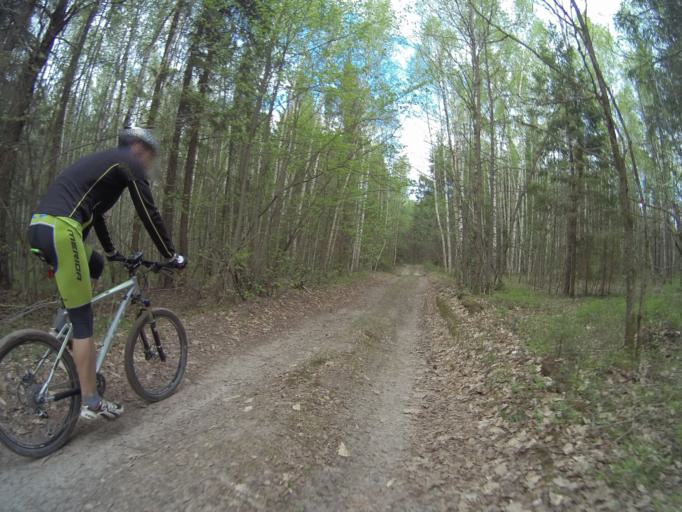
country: RU
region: Vladimir
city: Orgtrud
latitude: 56.1116
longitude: 40.6821
